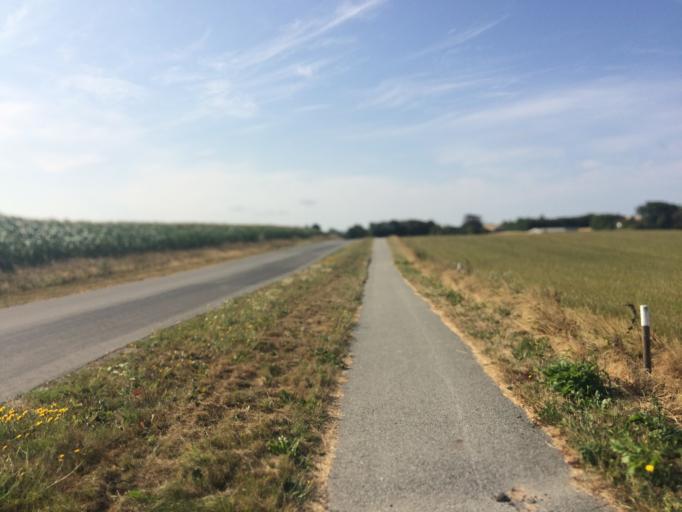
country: DK
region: Central Jutland
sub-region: Holstebro Kommune
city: Vinderup
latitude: 56.6047
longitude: 8.7715
